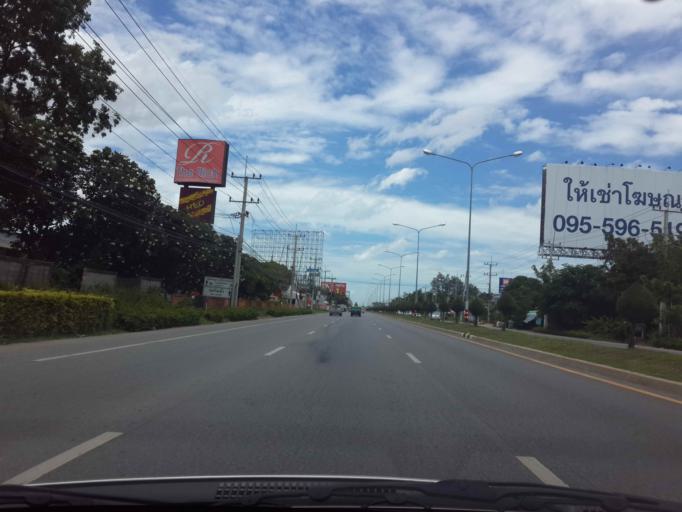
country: TH
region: Prachuap Khiri Khan
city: Hua Hin
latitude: 12.6523
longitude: 99.9518
